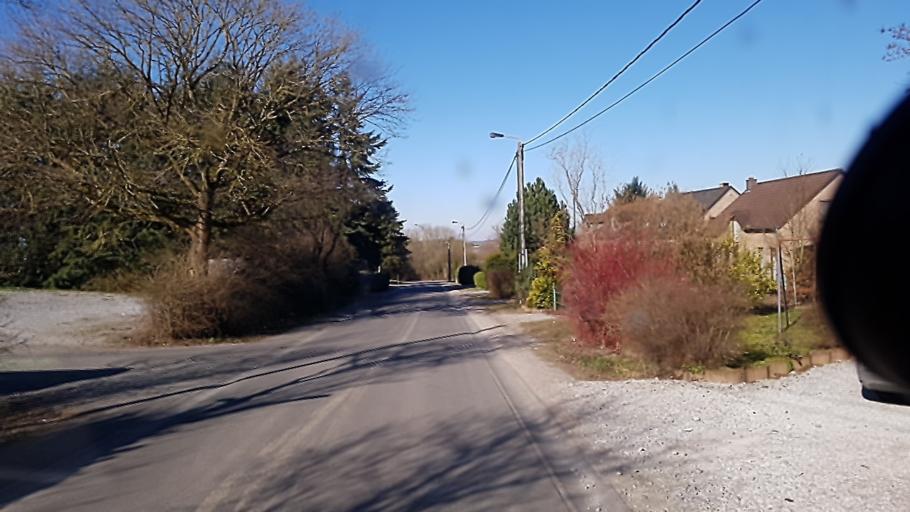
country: BE
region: Wallonia
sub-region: Province de Namur
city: Philippeville
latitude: 50.1973
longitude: 4.5389
